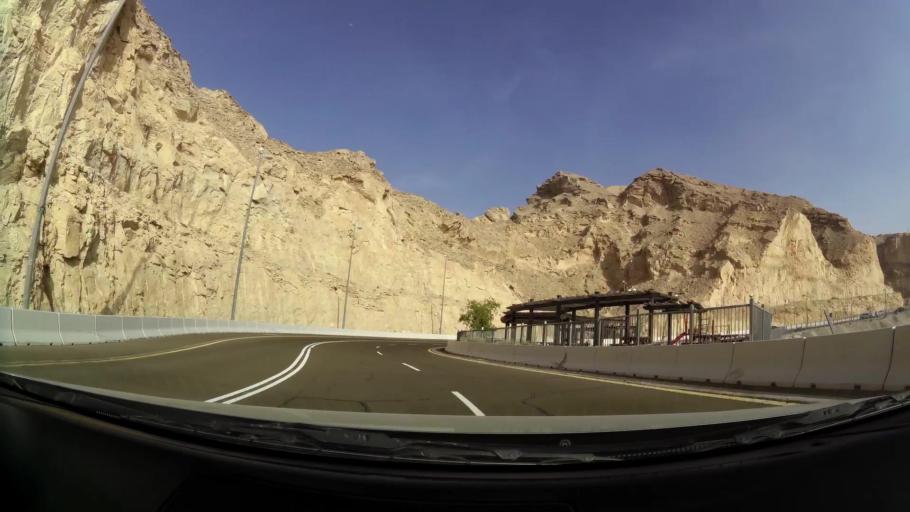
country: AE
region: Abu Dhabi
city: Al Ain
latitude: 24.0992
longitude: 55.7587
